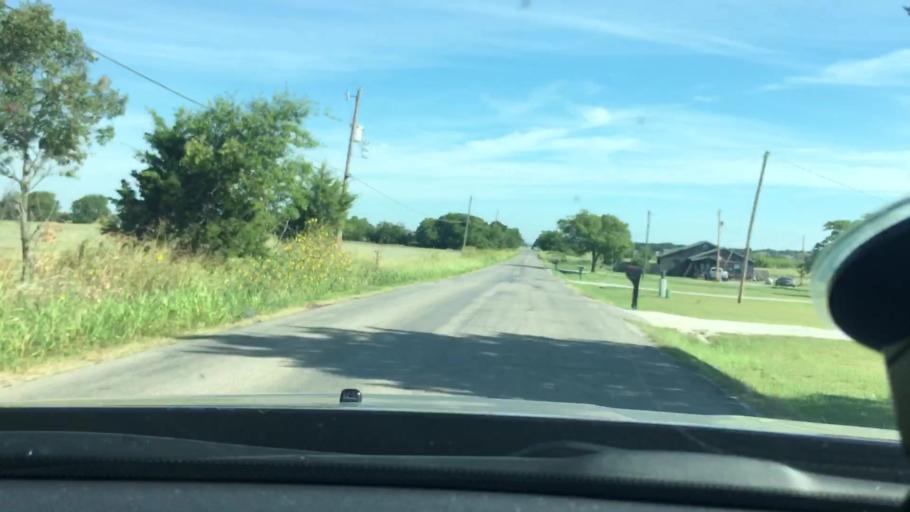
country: US
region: Oklahoma
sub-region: Carter County
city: Lone Grove
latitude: 34.1954
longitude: -97.2475
